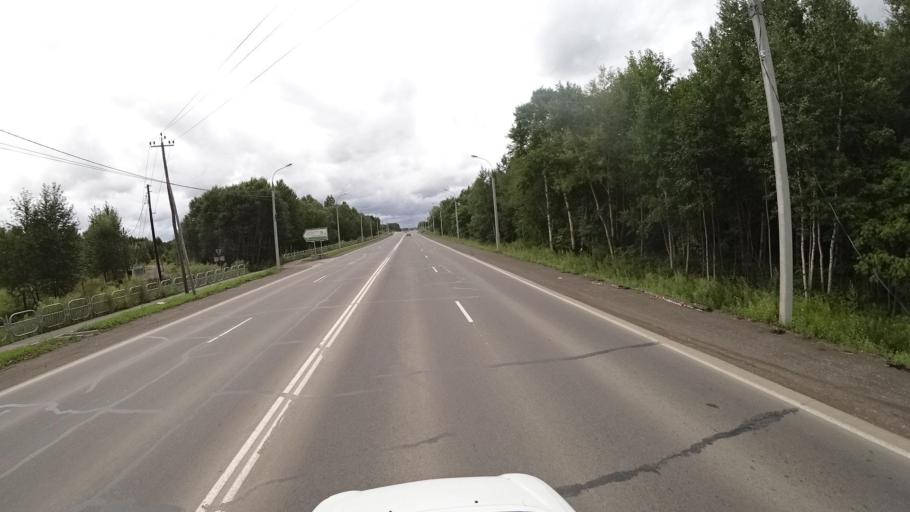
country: RU
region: Khabarovsk Krai
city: Solnechnyy
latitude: 50.5848
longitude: 137.0232
